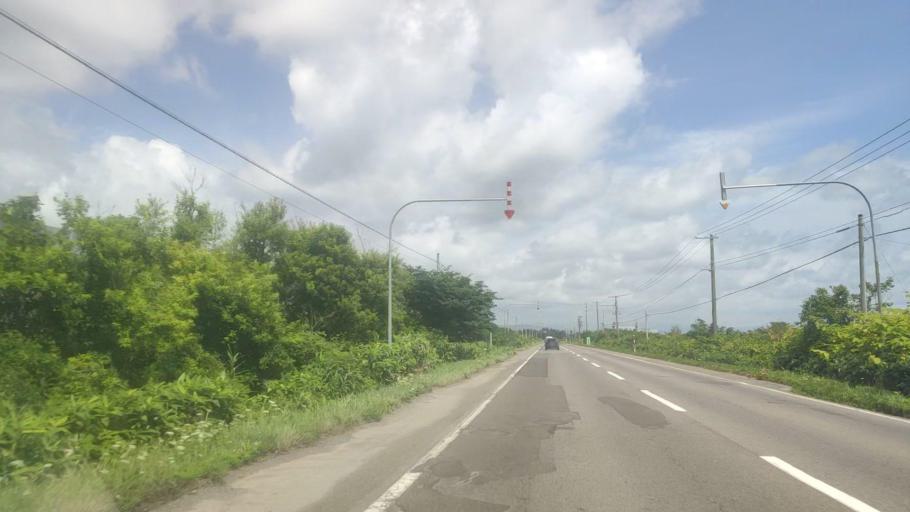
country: JP
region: Hokkaido
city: Niseko Town
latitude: 42.4638
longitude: 140.3385
